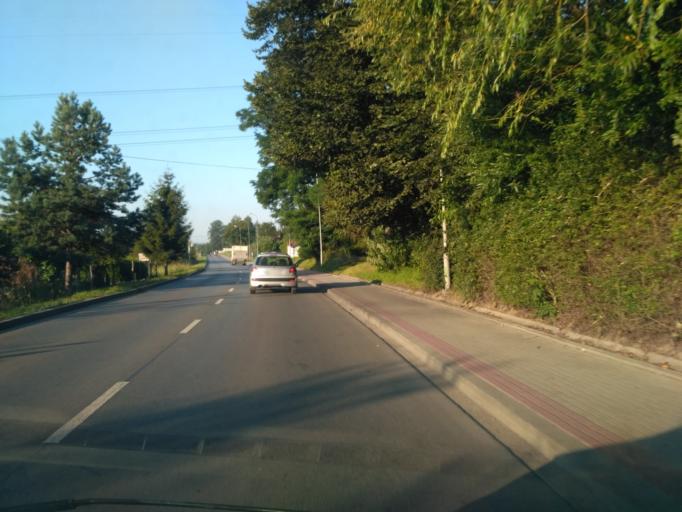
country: PL
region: Subcarpathian Voivodeship
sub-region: Powiat krosnienski
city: Korczyna
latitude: 49.7080
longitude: 21.7896
